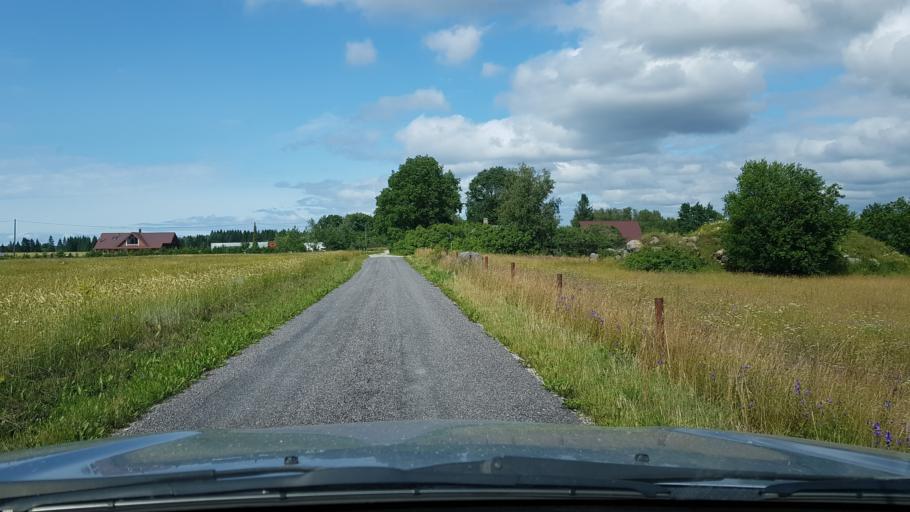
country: EE
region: Ida-Virumaa
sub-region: Narva-Joesuu linn
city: Narva-Joesuu
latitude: 59.3703
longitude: 27.9541
